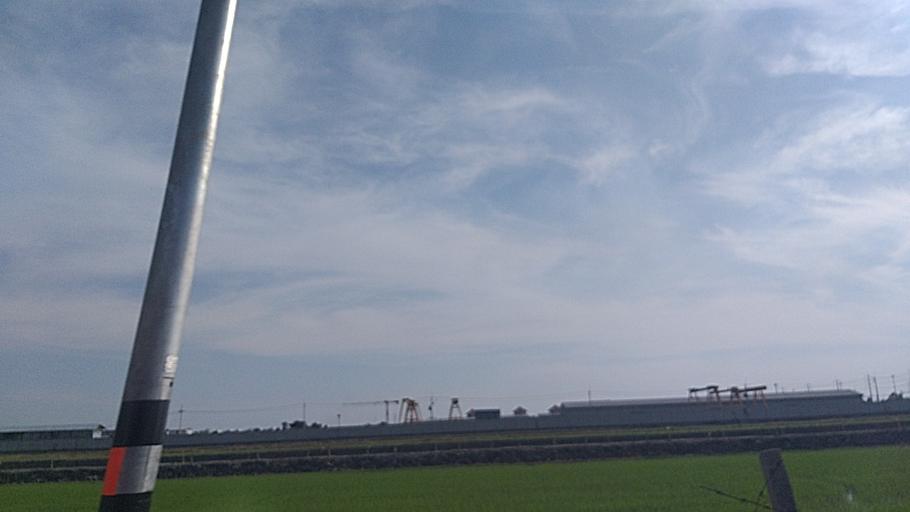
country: TH
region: Pathum Thani
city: Lam Luk Ka
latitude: 13.9616
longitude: 100.7153
